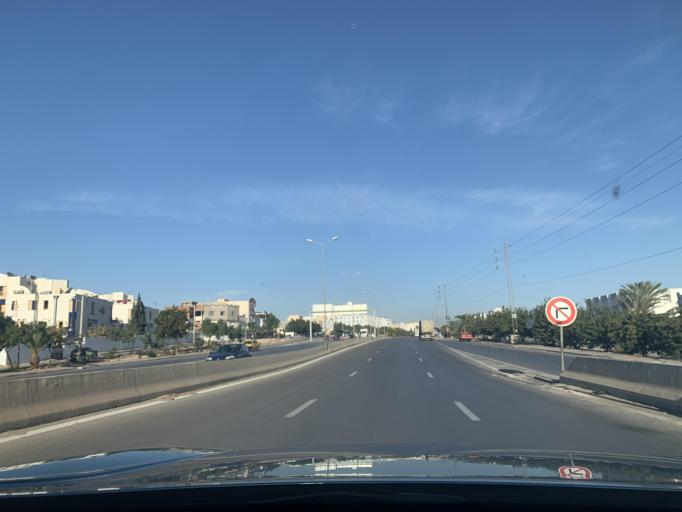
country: DZ
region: Souk Ahras
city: Souk Ahras
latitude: 36.3675
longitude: 8.0004
